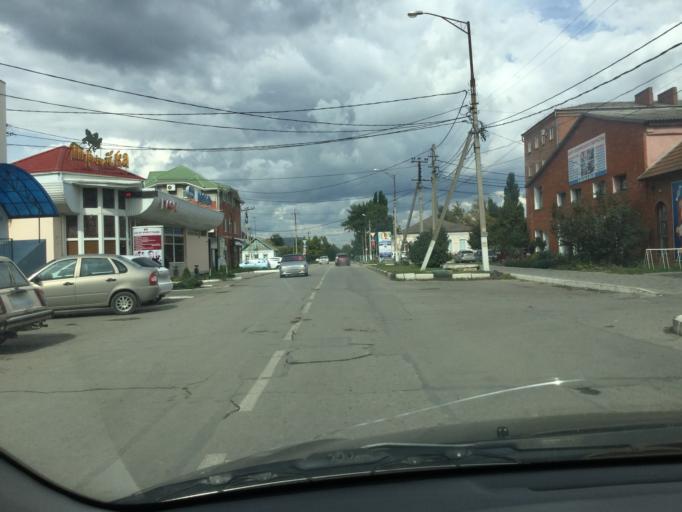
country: RU
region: Krasnodarskiy
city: Slavyansk-na-Kubani
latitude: 45.2577
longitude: 38.1212
